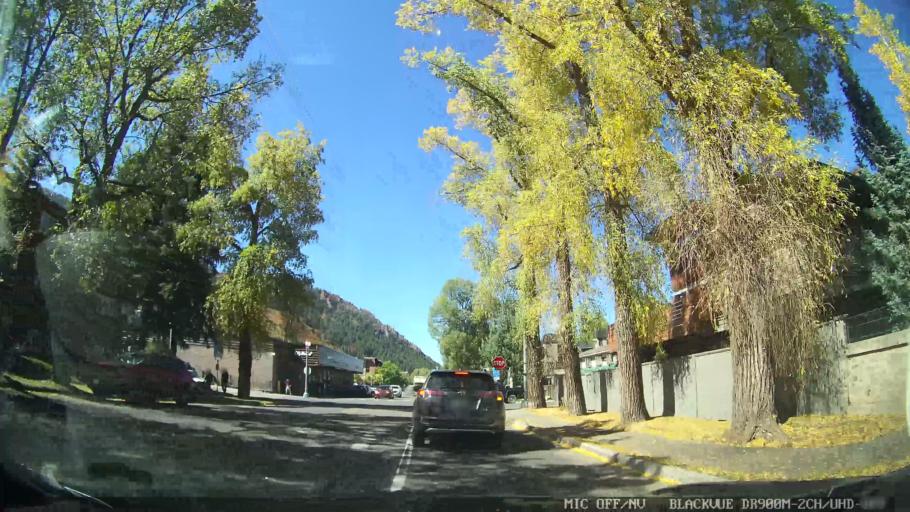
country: US
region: Colorado
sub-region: Pitkin County
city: Aspen
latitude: 39.1872
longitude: -106.8148
